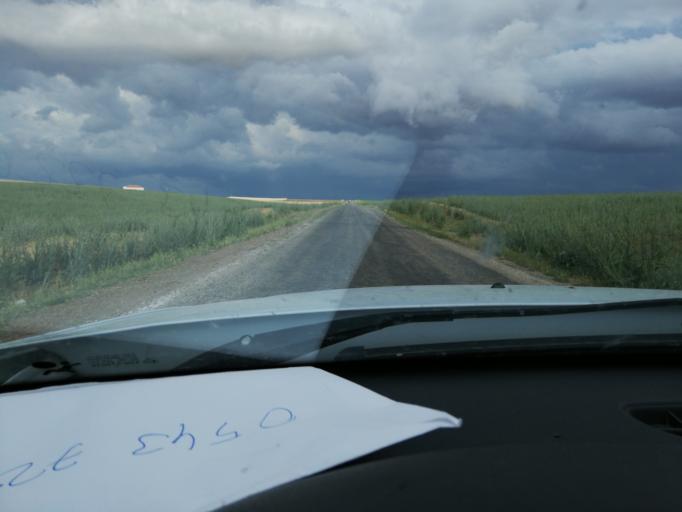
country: TR
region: Kirsehir
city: Kirsehir
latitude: 39.0424
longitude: 34.1687
